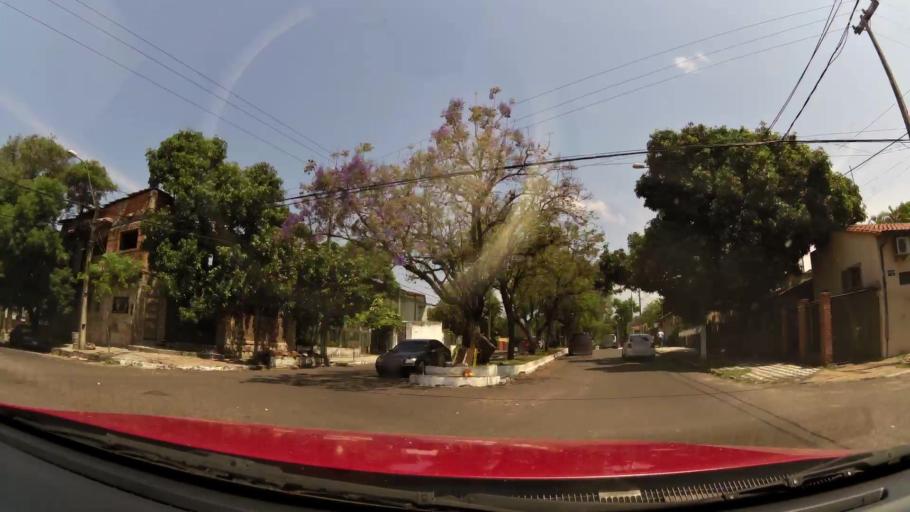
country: PY
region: Asuncion
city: Asuncion
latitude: -25.2959
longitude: -57.6323
